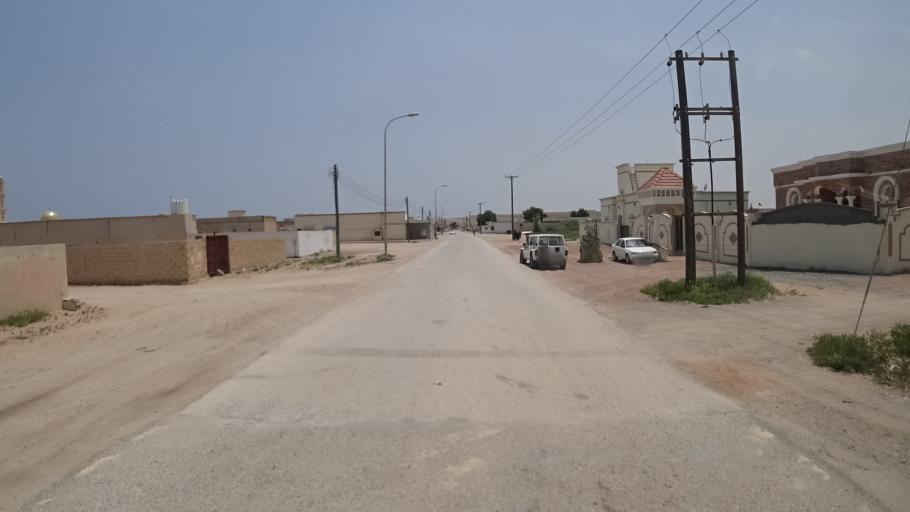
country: OM
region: Ash Sharqiyah
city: Sur
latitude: 22.5122
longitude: 59.7981
